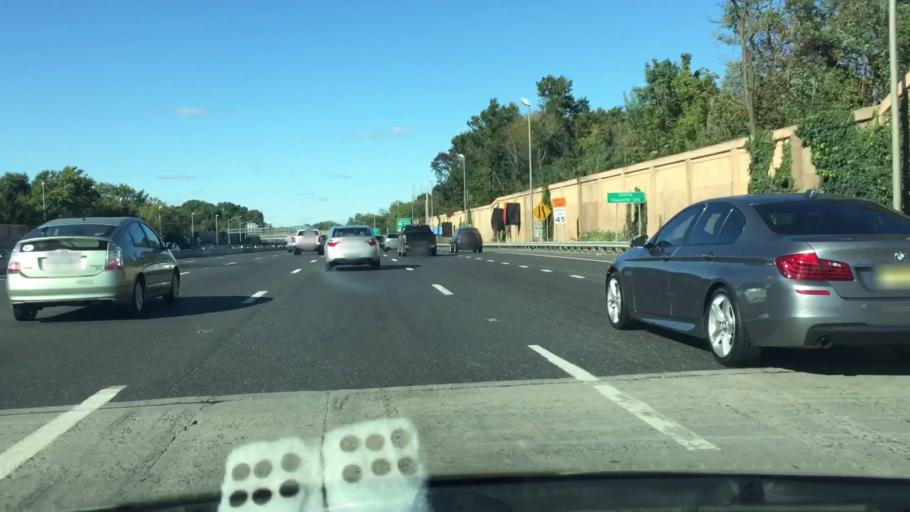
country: US
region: New Jersey
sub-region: Camden County
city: Mount Ephraim
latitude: 39.8792
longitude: -75.1026
